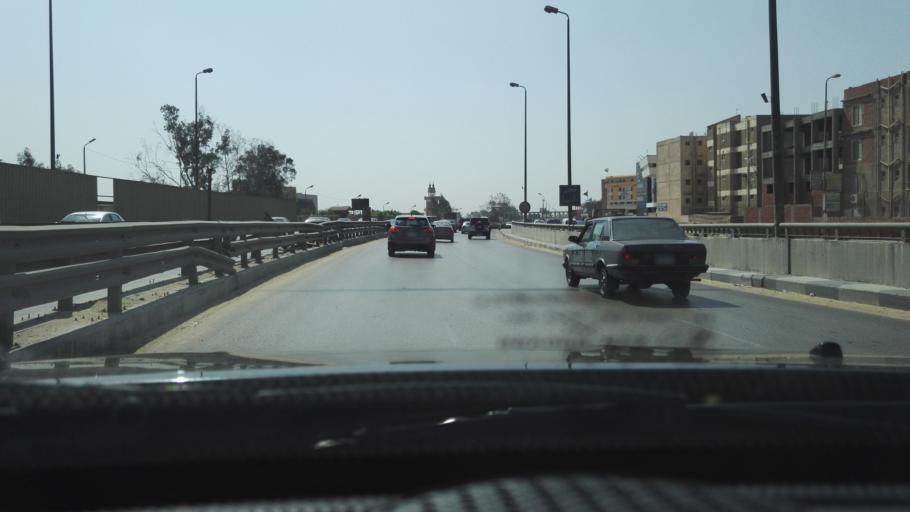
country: EG
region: Muhafazat al Qahirah
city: Cairo
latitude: 30.0789
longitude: 31.3771
